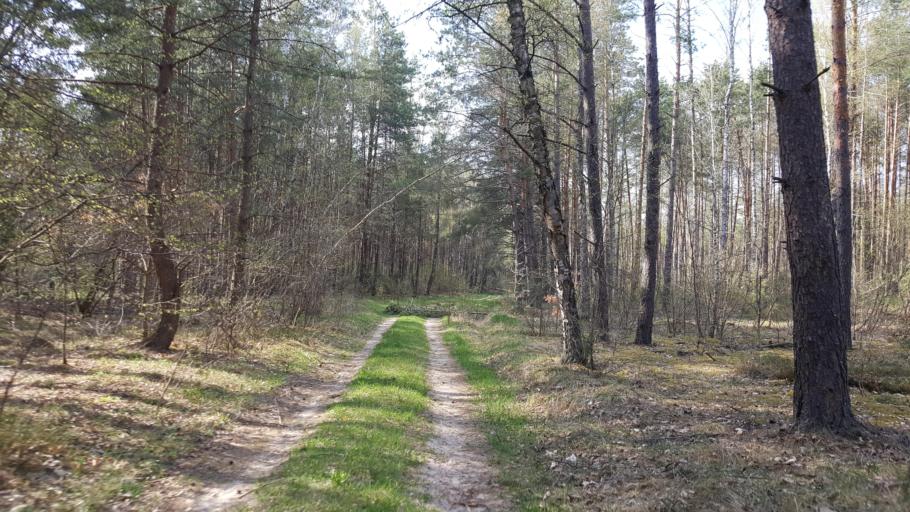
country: BY
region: Brest
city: Kamyanyets
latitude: 52.3478
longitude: 23.8433
